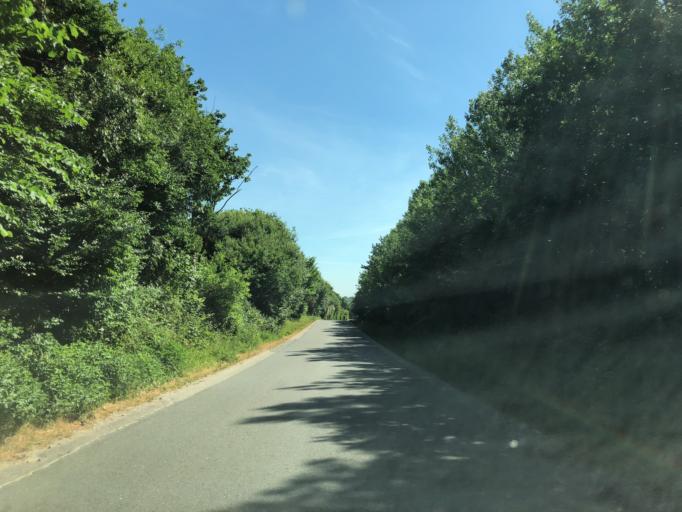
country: DK
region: Central Jutland
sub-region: Struer Kommune
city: Struer
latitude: 56.4353
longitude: 8.4946
